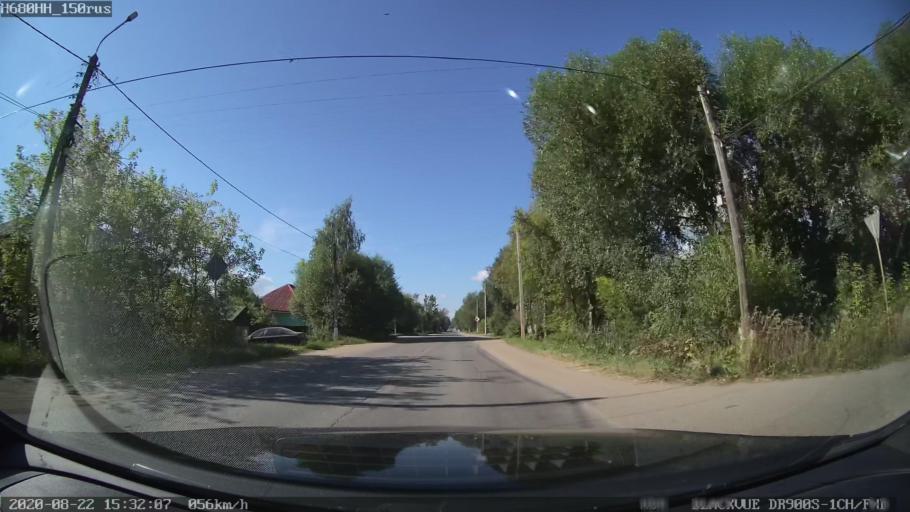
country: RU
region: Tverskaya
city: Bezhetsk
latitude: 57.7666
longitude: 36.7083
